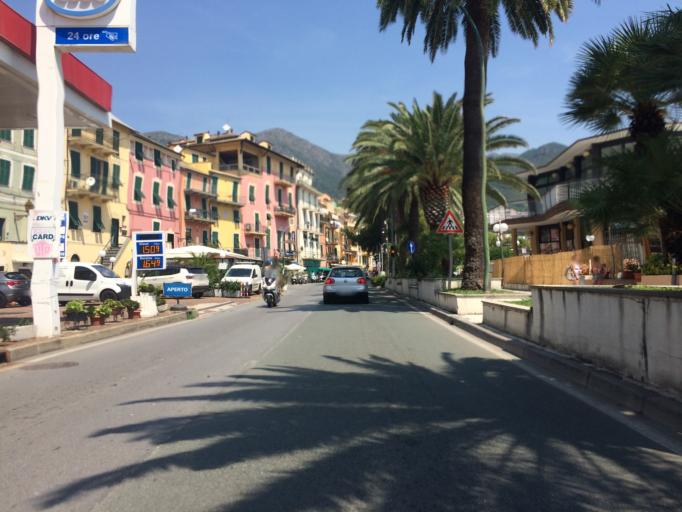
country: IT
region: Liguria
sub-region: Provincia di Genova
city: Arenzano
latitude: 44.4026
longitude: 8.6856
